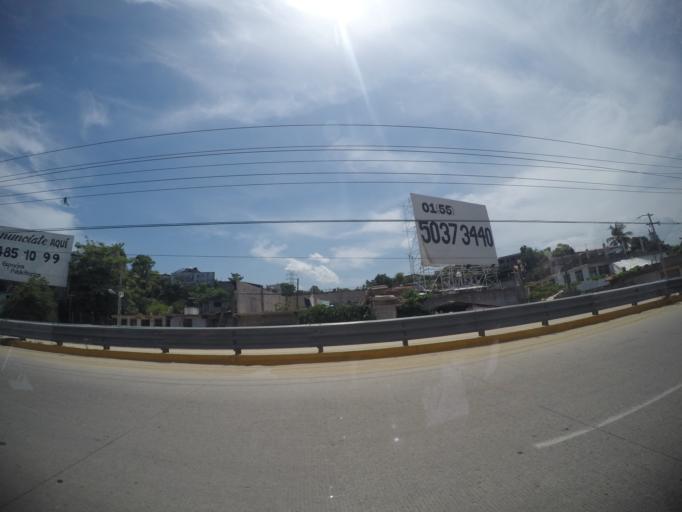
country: MX
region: Guerrero
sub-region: Acapulco de Juarez
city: Colonia Nueva Revolucion
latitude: 16.9123
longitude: -99.8249
